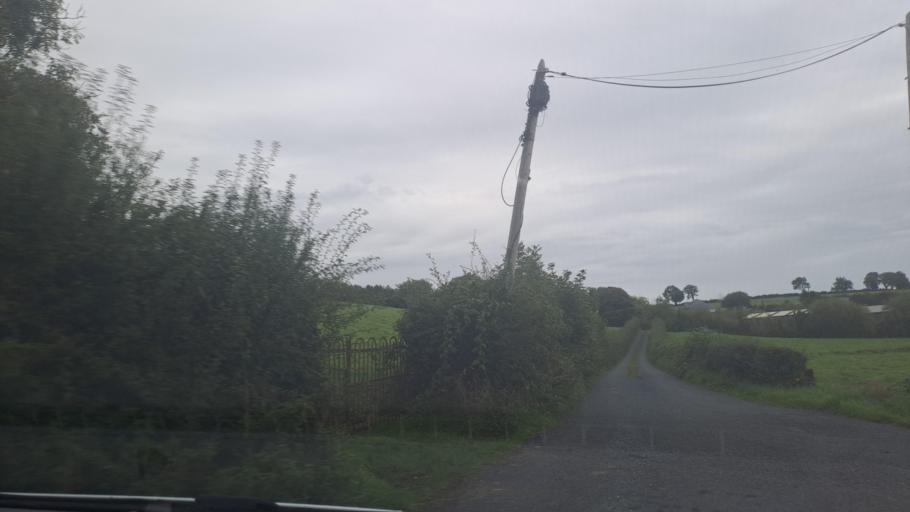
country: IE
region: Ulster
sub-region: County Monaghan
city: Carrickmacross
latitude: 53.9824
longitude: -6.7737
